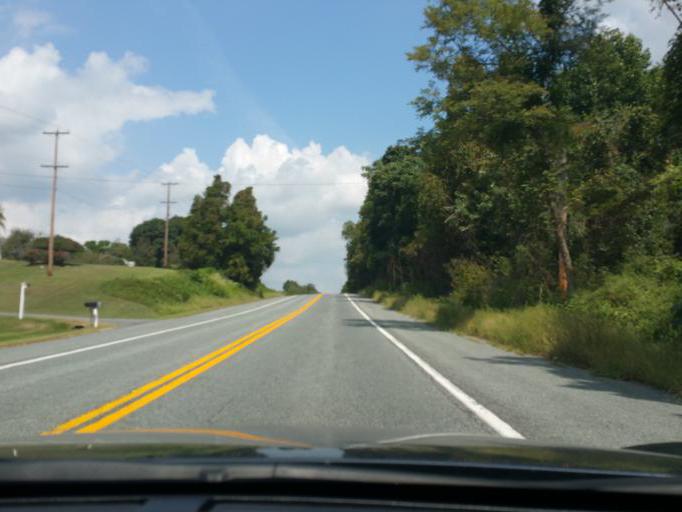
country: US
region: Maryland
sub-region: Cecil County
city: Perryville
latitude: 39.6127
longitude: -76.1077
